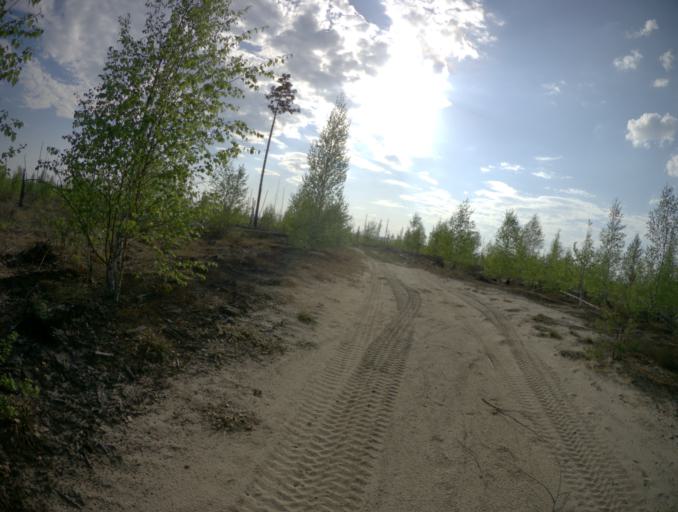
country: RU
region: Ivanovo
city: Talitsy
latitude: 56.4111
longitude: 42.2434
